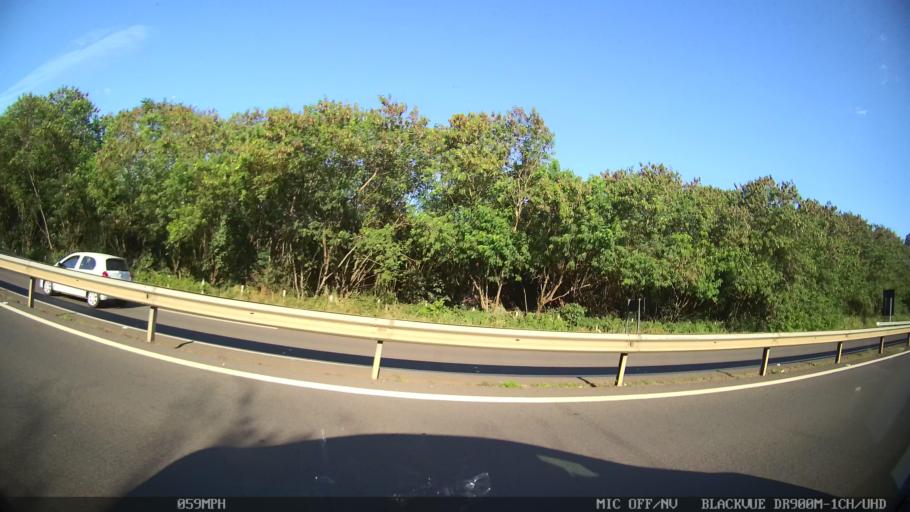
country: BR
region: Sao Paulo
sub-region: Piracicaba
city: Piracicaba
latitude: -22.6974
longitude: -47.6382
